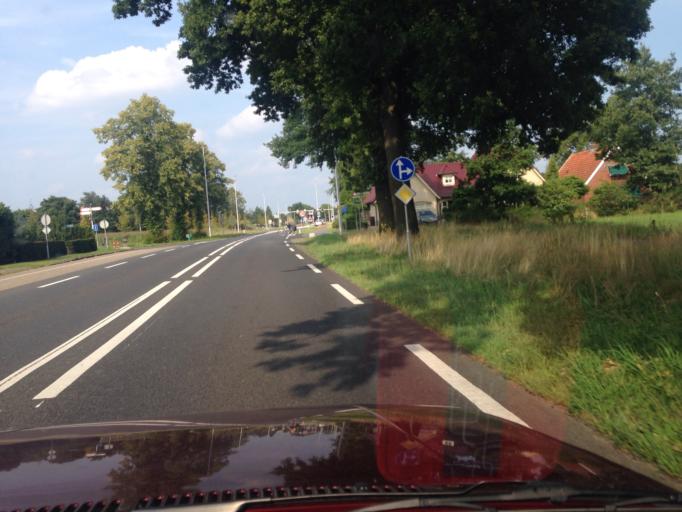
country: NL
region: Overijssel
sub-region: Gemeente Haaksbergen
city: Haaksbergen
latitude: 52.1651
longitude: 6.7645
